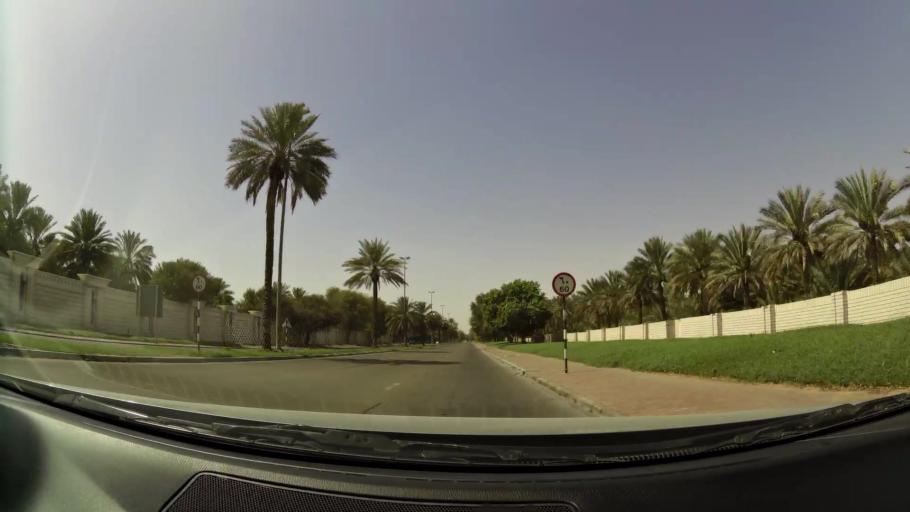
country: OM
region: Al Buraimi
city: Al Buraymi
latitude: 24.2939
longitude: 55.7677
